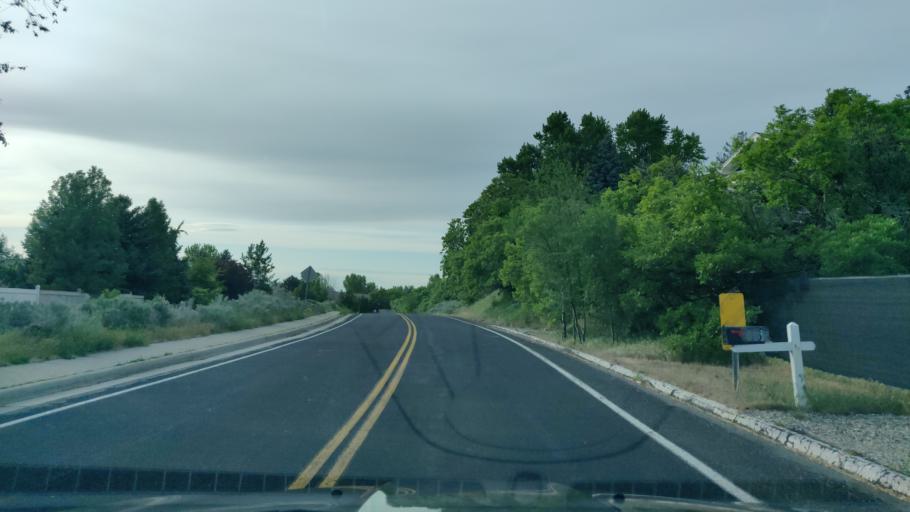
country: US
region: Utah
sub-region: Salt Lake County
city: Granite
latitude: 40.5901
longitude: -111.7988
